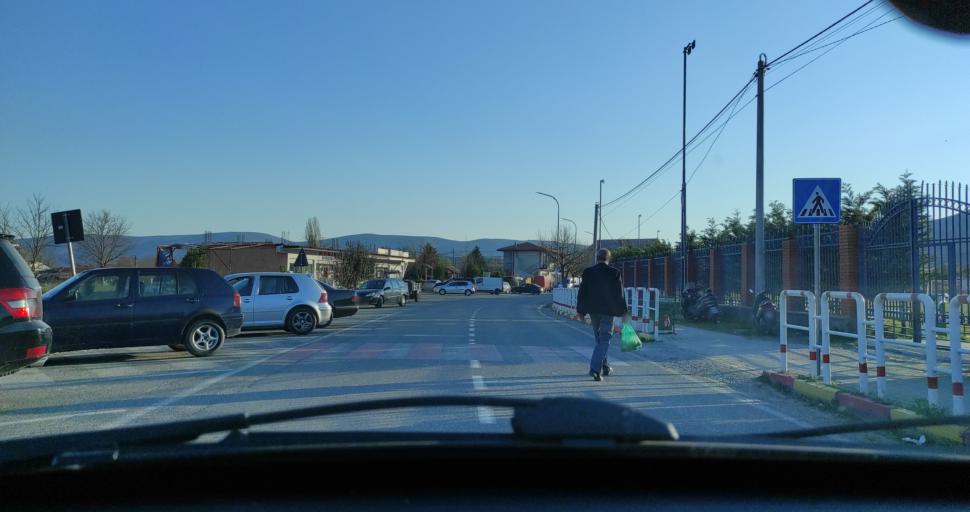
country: AL
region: Shkoder
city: Vukatane
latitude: 41.9607
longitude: 19.5362
